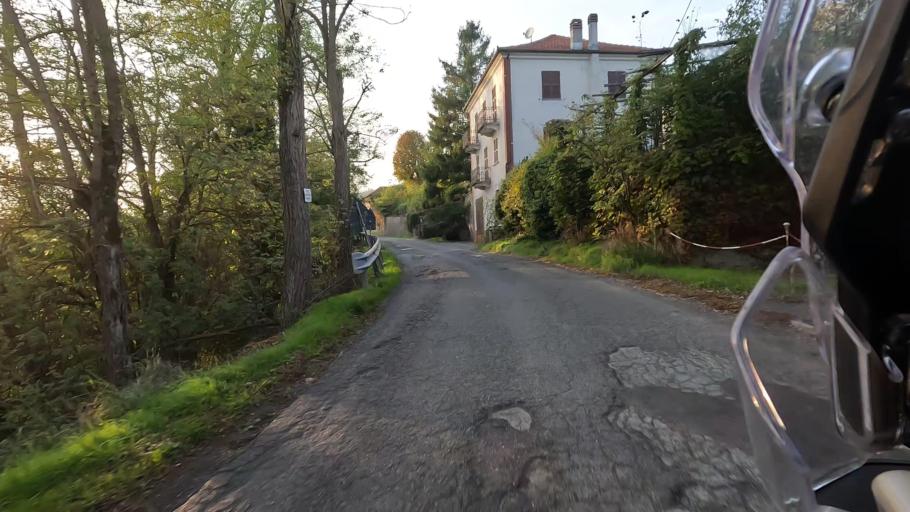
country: IT
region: Liguria
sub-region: Provincia di Savona
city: Mioglia
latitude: 44.5132
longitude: 8.4524
